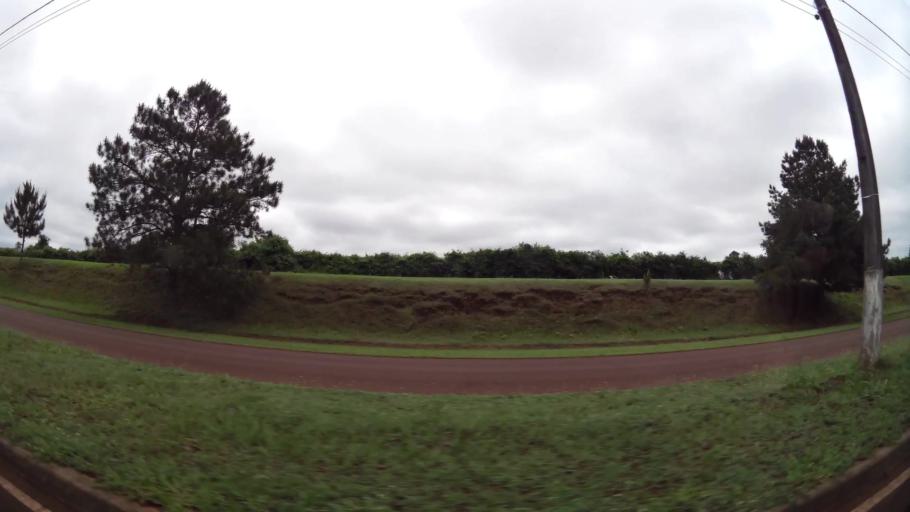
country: PY
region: Alto Parana
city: Colonia Yguazu
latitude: -25.4656
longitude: -54.8468
